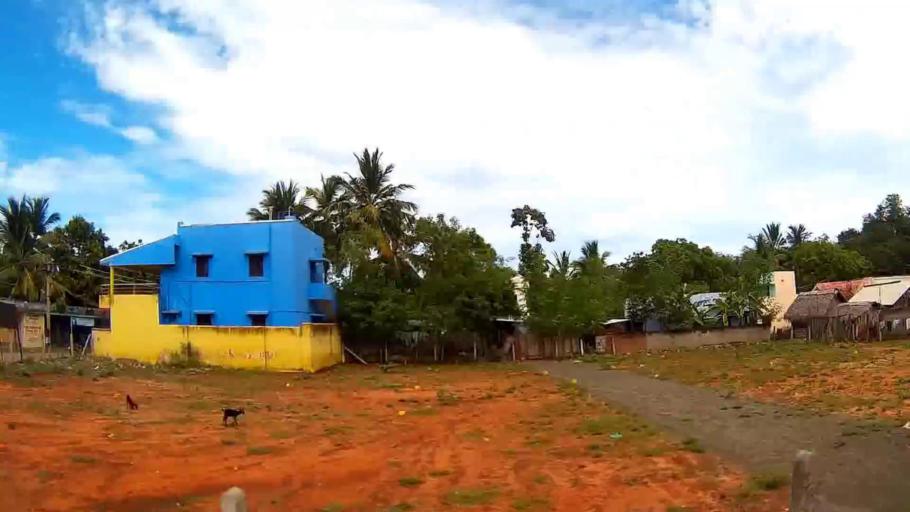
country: VN
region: Lao Cai
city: Sa Pa
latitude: 22.3345
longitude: 103.8416
